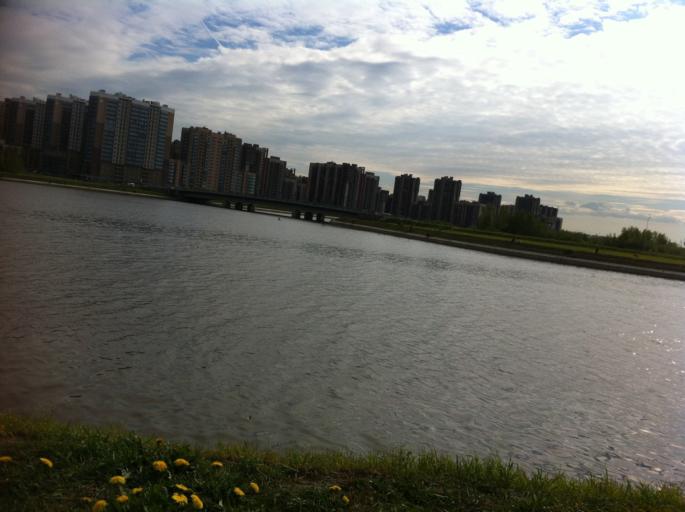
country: RU
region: St.-Petersburg
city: Uritsk
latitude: 59.8582
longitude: 30.1593
